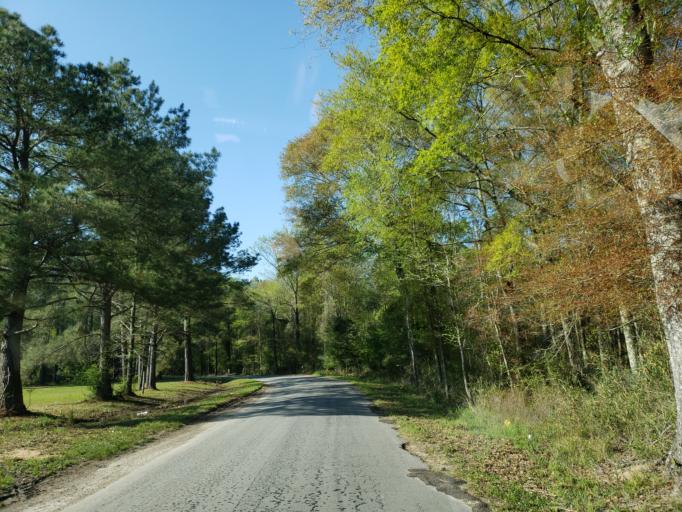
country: US
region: Mississippi
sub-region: Smith County
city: Taylorsville
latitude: 31.7012
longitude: -89.4143
